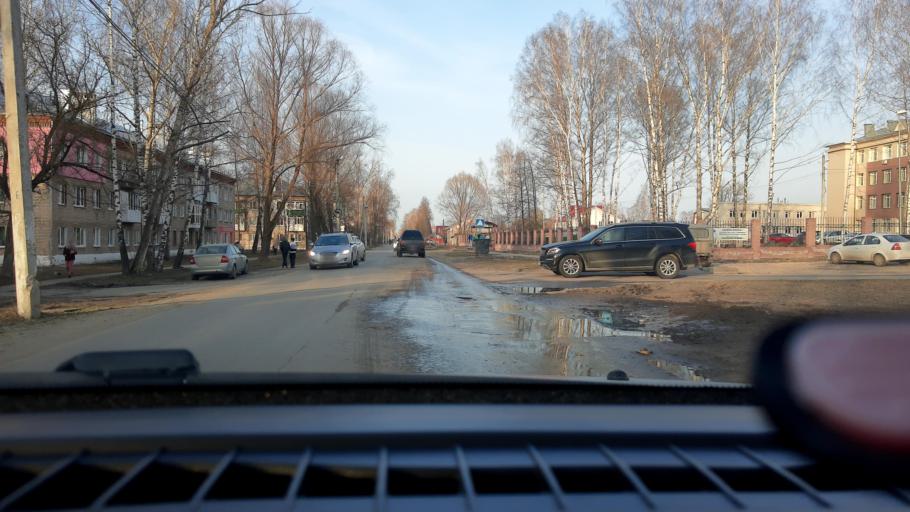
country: RU
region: Nizjnij Novgorod
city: Bogorodsk
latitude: 56.1038
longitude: 43.4850
